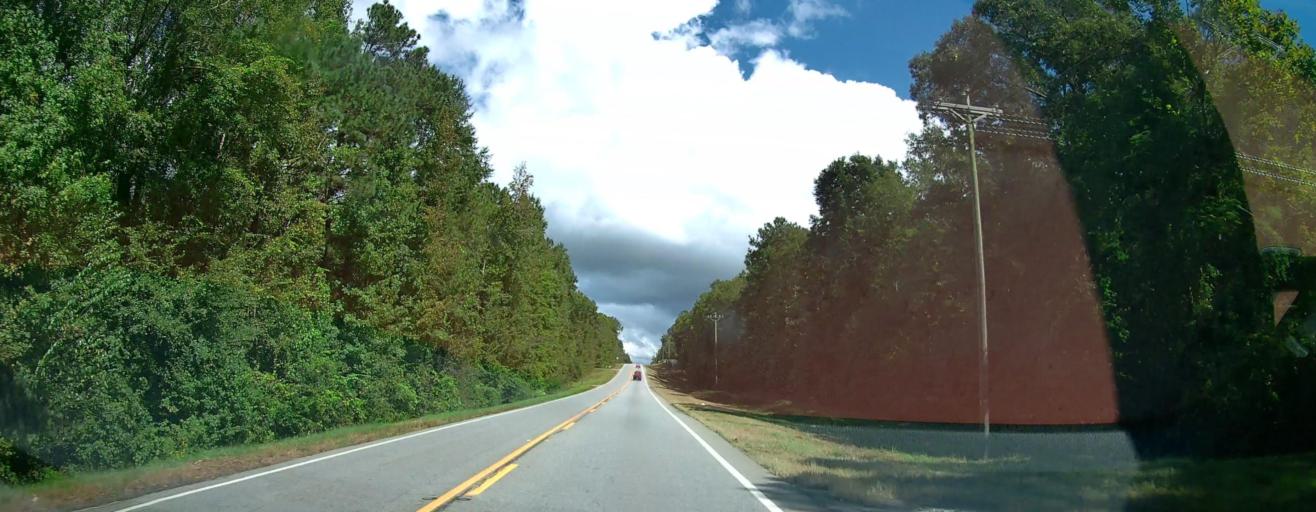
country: US
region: Georgia
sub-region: Jones County
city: Gray
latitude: 32.9486
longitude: -83.4606
